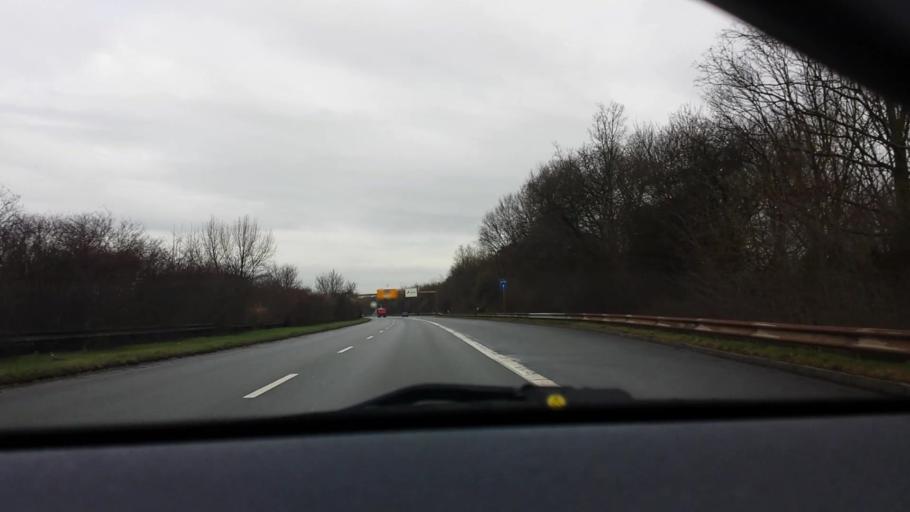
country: DE
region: North Rhine-Westphalia
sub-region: Regierungsbezirk Dusseldorf
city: Dusseldorf
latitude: 51.1780
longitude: 6.8074
